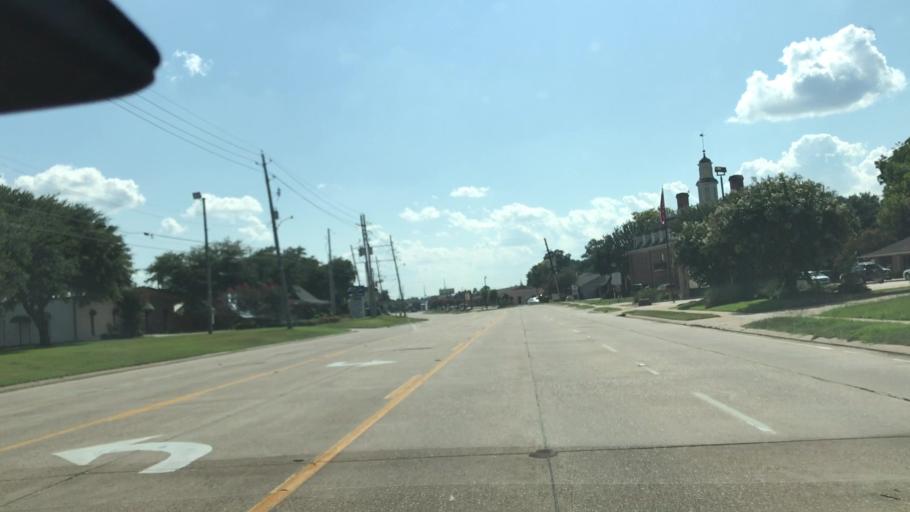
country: US
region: Louisiana
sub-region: Bossier Parish
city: Bossier City
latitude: 32.4451
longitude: -93.7058
